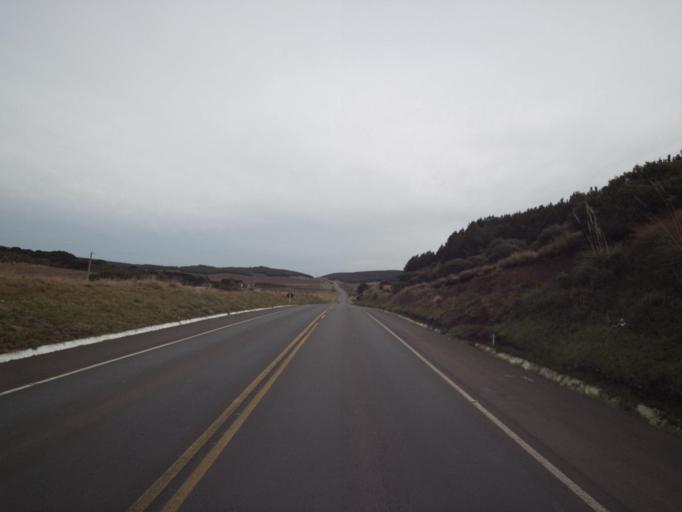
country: BR
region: Parana
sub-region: Palmas
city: Palmas
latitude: -26.6569
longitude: -51.5342
